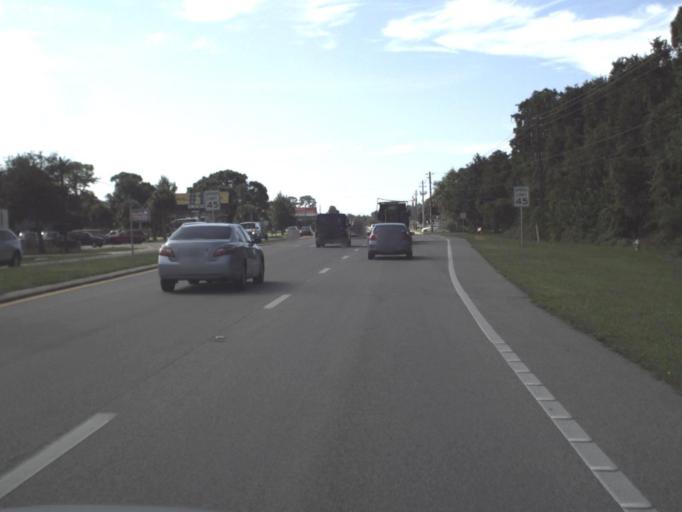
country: US
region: Florida
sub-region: Sarasota County
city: Osprey
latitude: 27.2036
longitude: -82.4904
